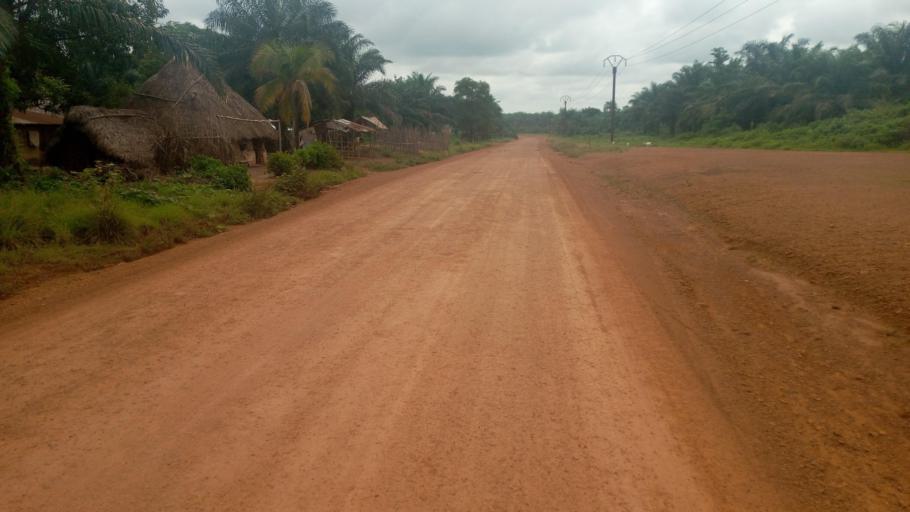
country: SL
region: Southern Province
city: Mogbwemo
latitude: 7.7244
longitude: -12.2812
